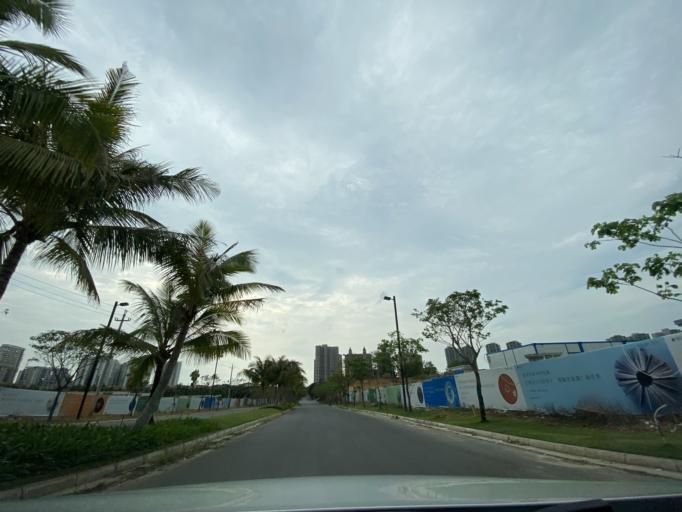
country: CN
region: Hainan
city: Yingzhou
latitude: 18.4199
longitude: 109.8879
